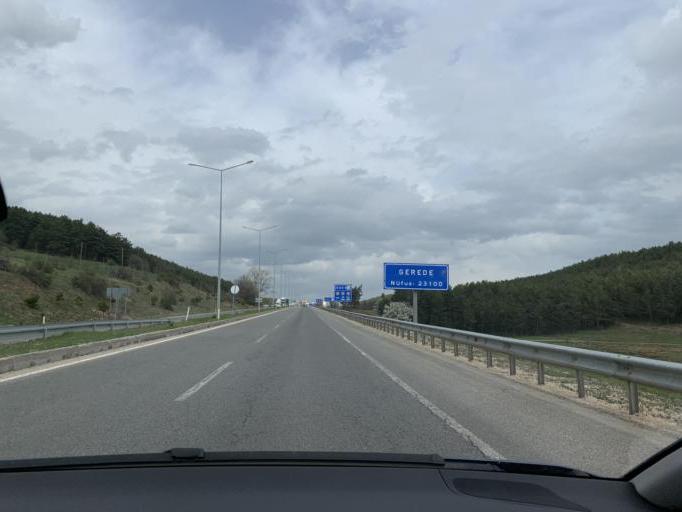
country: TR
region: Bolu
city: Gerede
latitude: 40.7985
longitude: 32.1709
